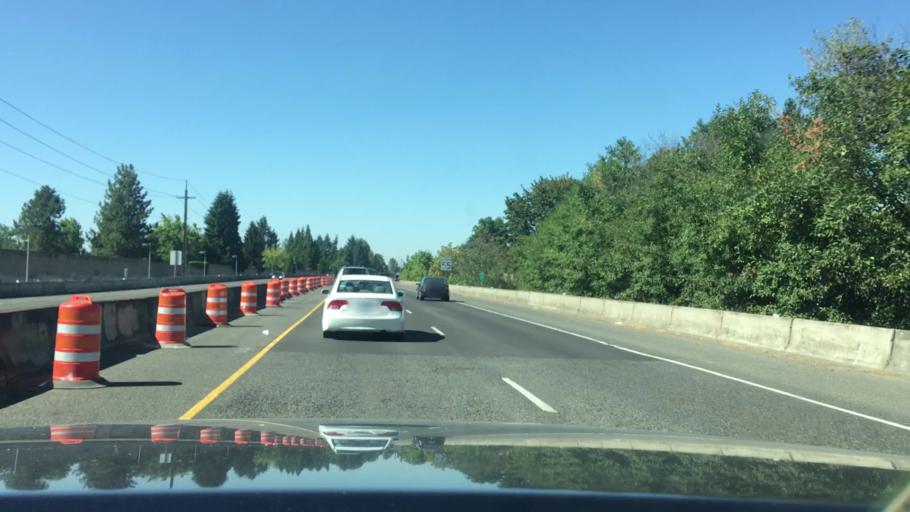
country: US
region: Oregon
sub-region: Lane County
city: Eugene
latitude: 44.0749
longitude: -123.1735
